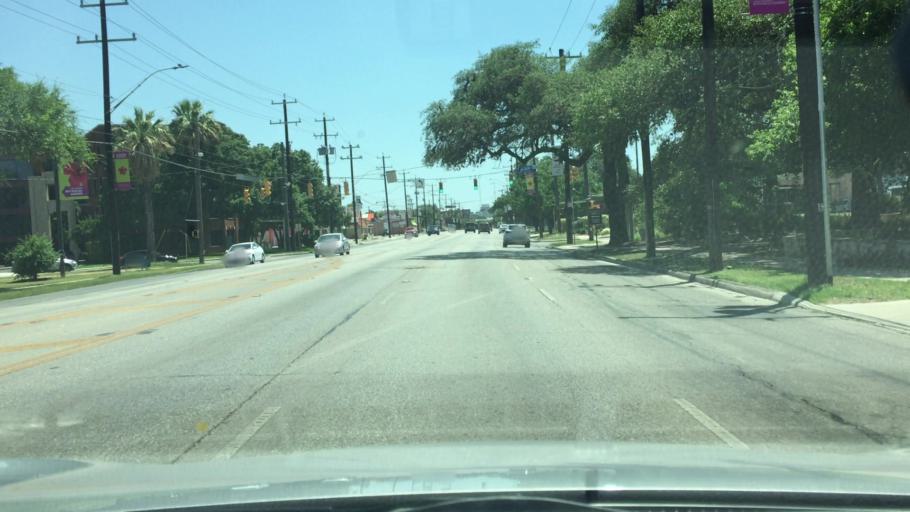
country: US
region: Texas
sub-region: Bexar County
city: Terrell Hills
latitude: 29.4583
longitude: -98.4687
